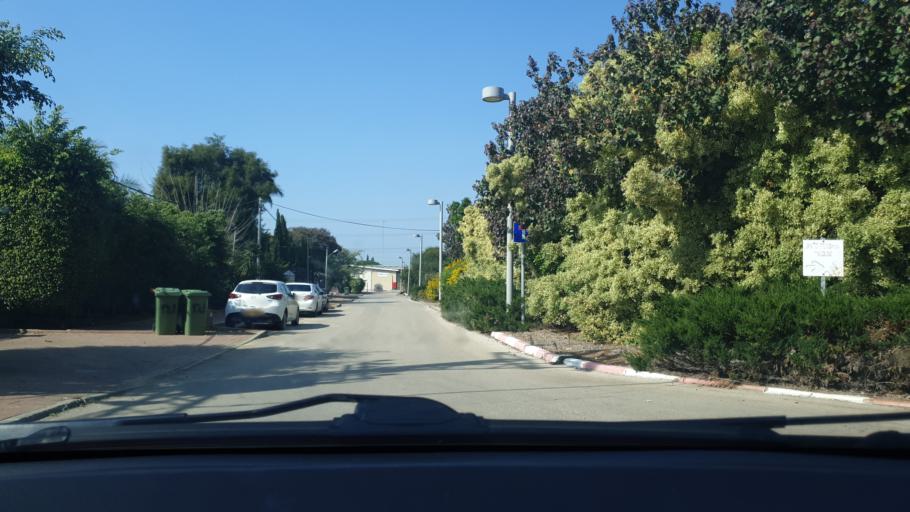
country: IL
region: Central District
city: Bet Dagan
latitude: 32.0095
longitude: 34.8186
